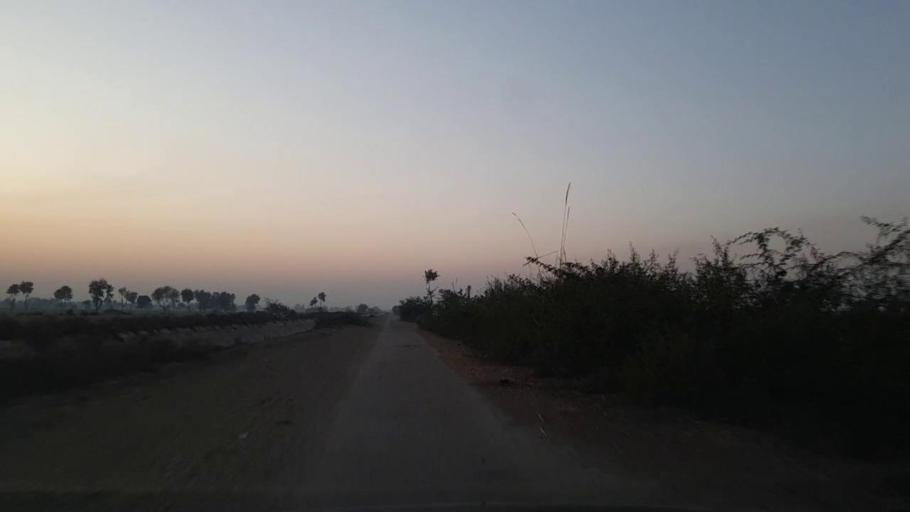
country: PK
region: Sindh
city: Daur
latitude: 26.4814
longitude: 68.4861
